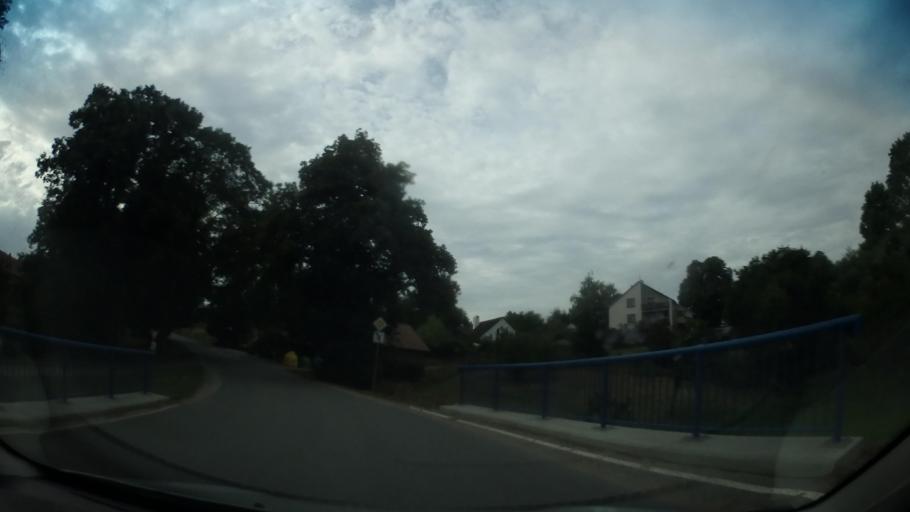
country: CZ
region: Pardubicky
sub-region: Okres Chrudim
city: Sec
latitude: 49.8140
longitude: 15.7209
